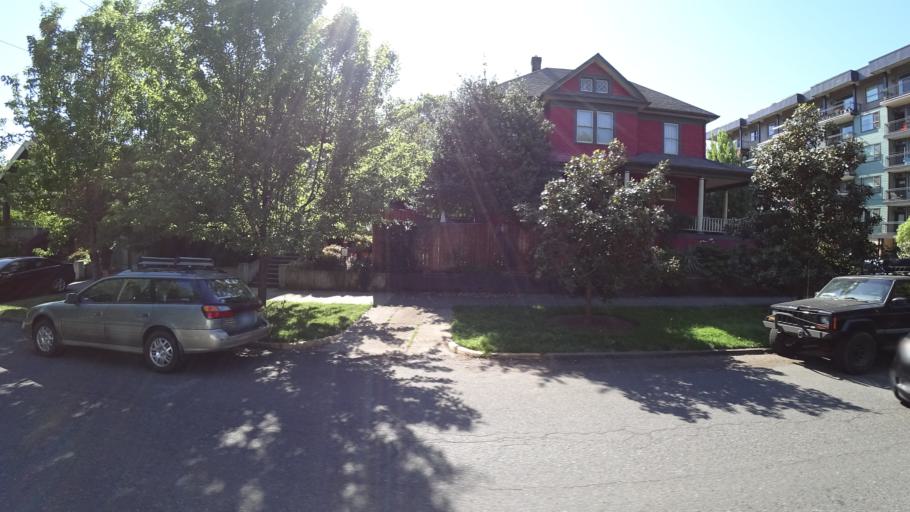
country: US
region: Oregon
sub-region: Multnomah County
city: Portland
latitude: 45.5410
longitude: -122.6586
